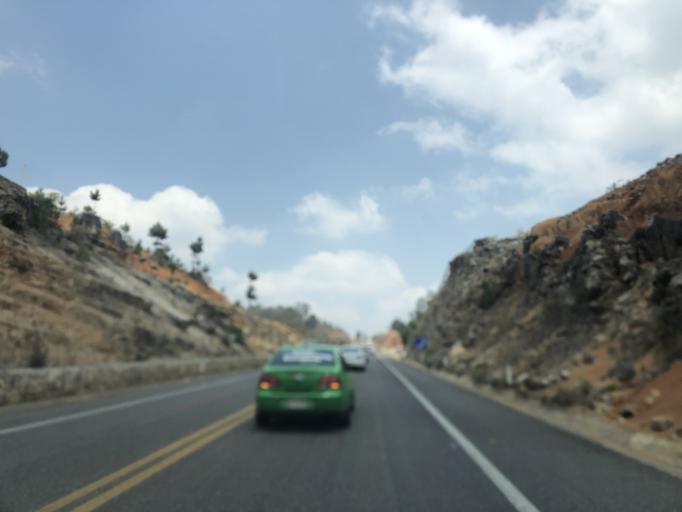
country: MX
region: Chiapas
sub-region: Zinacantan
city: Nachig
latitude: 16.6895
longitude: -92.7266
